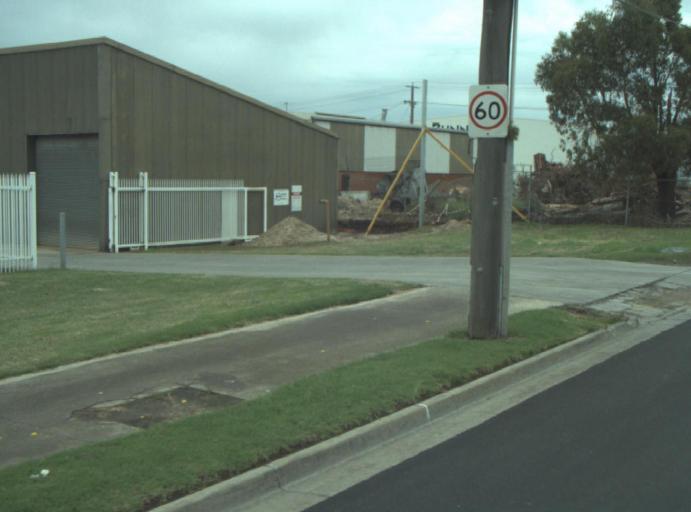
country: AU
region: Victoria
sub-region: Greater Geelong
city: Breakwater
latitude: -38.1858
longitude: 144.3699
